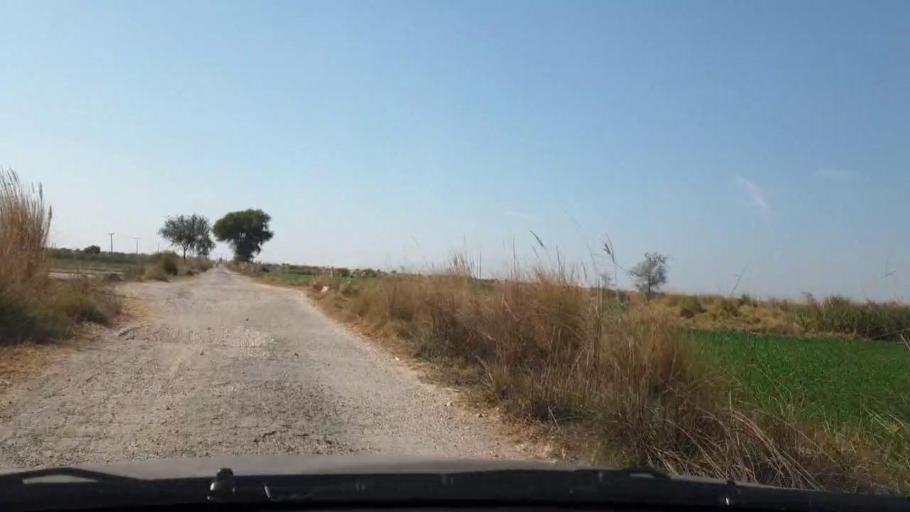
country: PK
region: Sindh
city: Khadro
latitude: 26.2678
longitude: 68.8037
